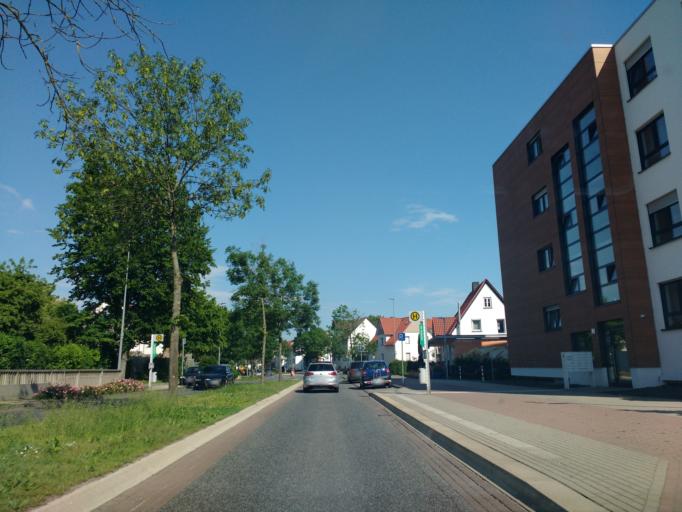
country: DE
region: Hesse
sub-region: Regierungsbezirk Kassel
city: Baunatal
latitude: 51.2587
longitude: 9.4124
